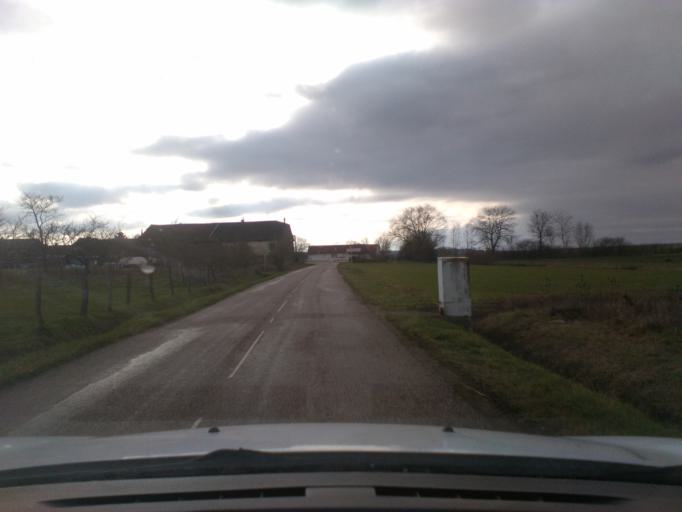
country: FR
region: Lorraine
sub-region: Departement des Vosges
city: Vittel
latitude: 48.3290
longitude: 5.9845
